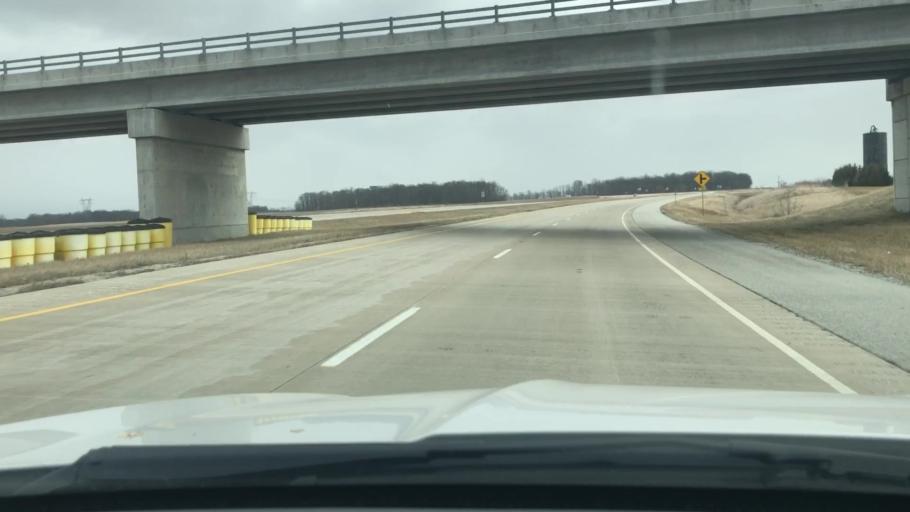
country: US
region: Indiana
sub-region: Carroll County
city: Delphi
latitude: 40.6224
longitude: -86.6208
